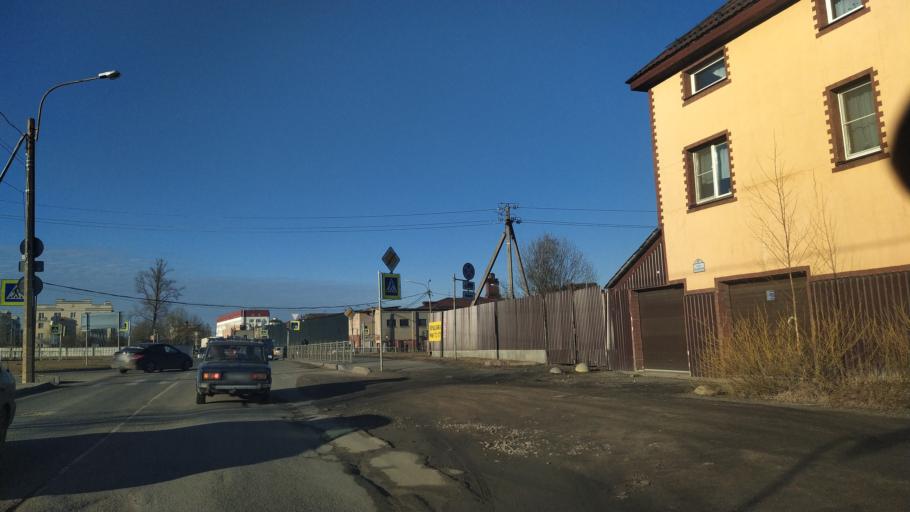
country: RU
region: St.-Petersburg
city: Pushkin
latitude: 59.6999
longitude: 30.3945
